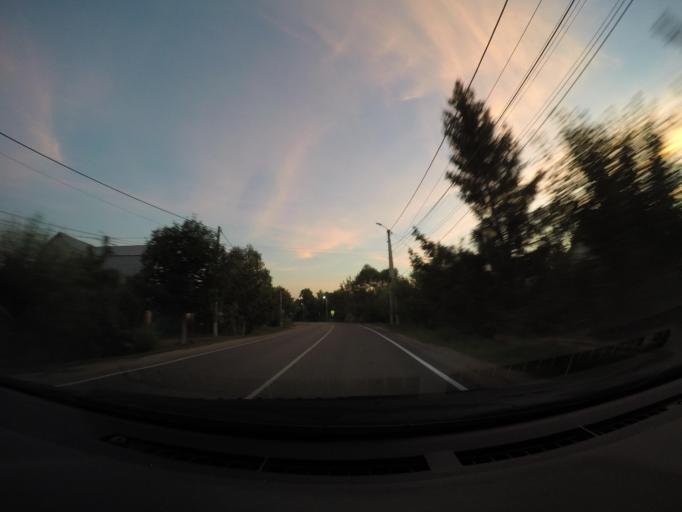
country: RU
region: Moskovskaya
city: Gzhel'
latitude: 55.5808
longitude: 38.3994
